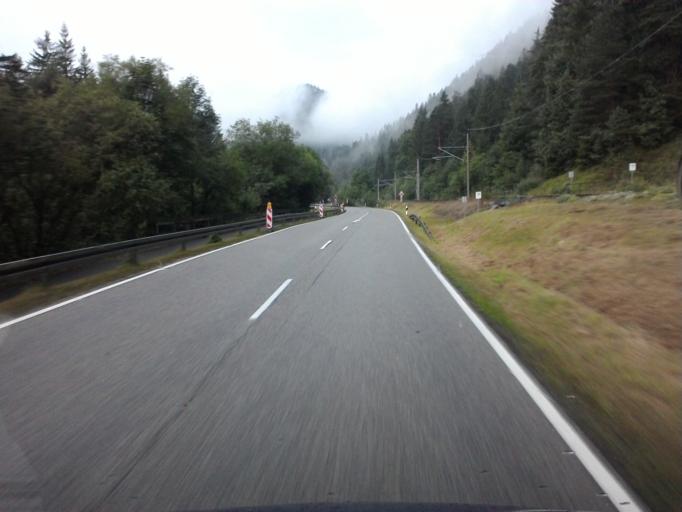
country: DE
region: Bavaria
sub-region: Upper Bavaria
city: Grainau
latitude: 47.4843
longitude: 10.9840
